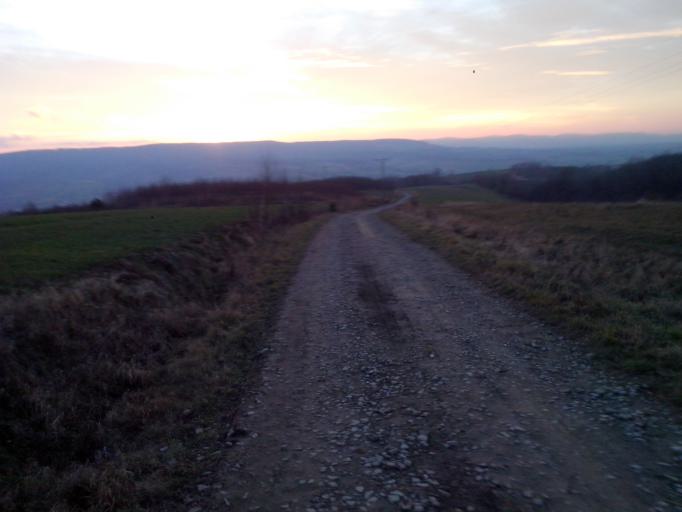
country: PL
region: Subcarpathian Voivodeship
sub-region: Powiat strzyzowski
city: Jawornik
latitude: 49.8488
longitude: 21.8471
